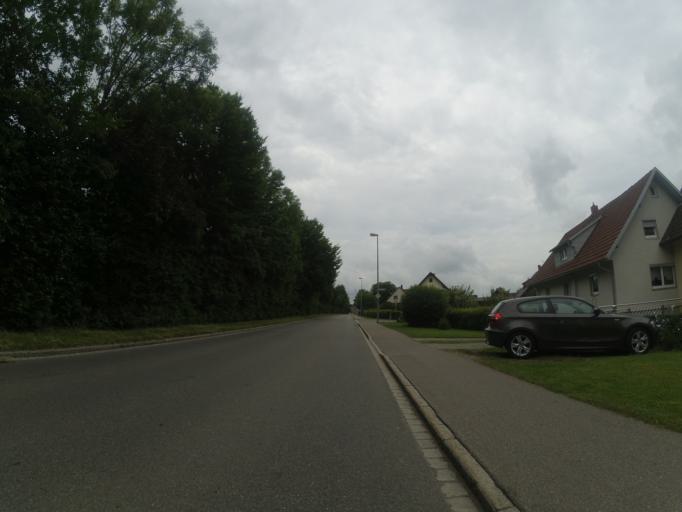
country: DE
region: Baden-Wuerttemberg
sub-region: Tuebingen Region
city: Wangen im Allgau
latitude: 47.6991
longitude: 9.8340
